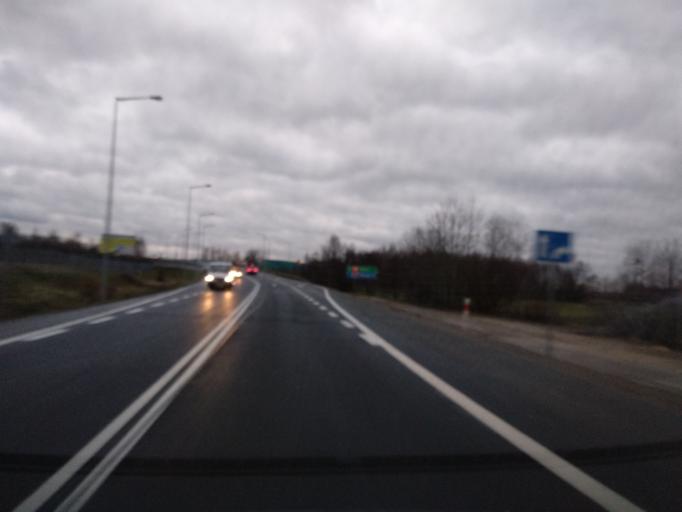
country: PL
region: Greater Poland Voivodeship
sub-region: Powiat koninski
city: Stare Miasto
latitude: 52.1667
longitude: 18.2087
